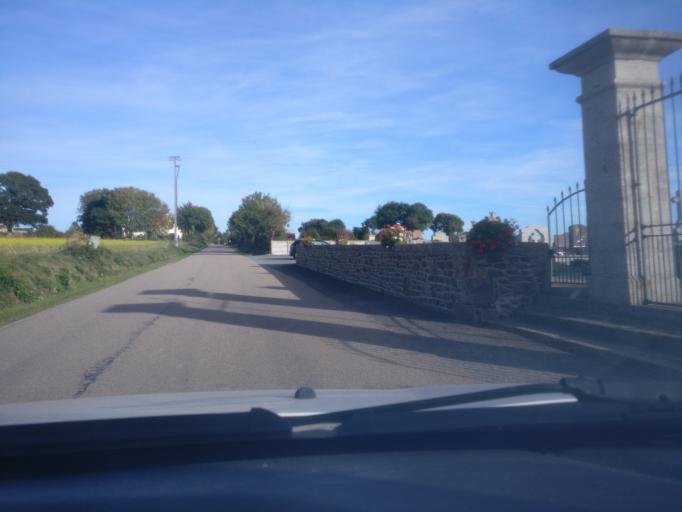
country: FR
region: Lower Normandy
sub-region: Departement de la Manche
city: Marcey-les-Greves
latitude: 48.6998
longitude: -1.4374
